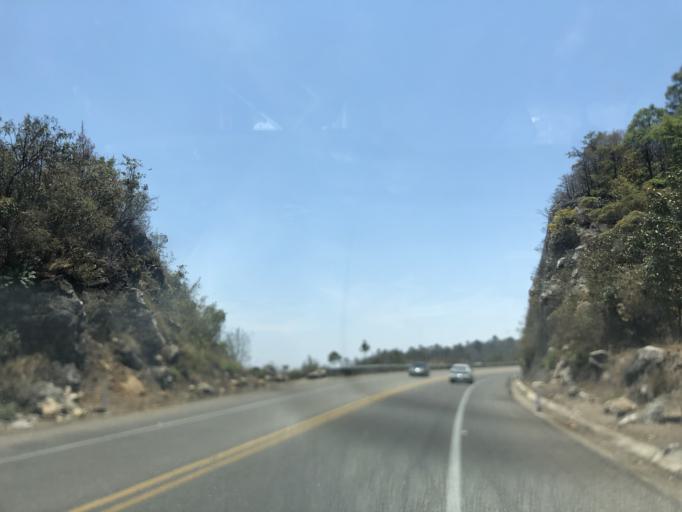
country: MX
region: Chiapas
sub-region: Zinacantan
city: Bochojbo Alto
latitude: 16.7068
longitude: -92.6902
